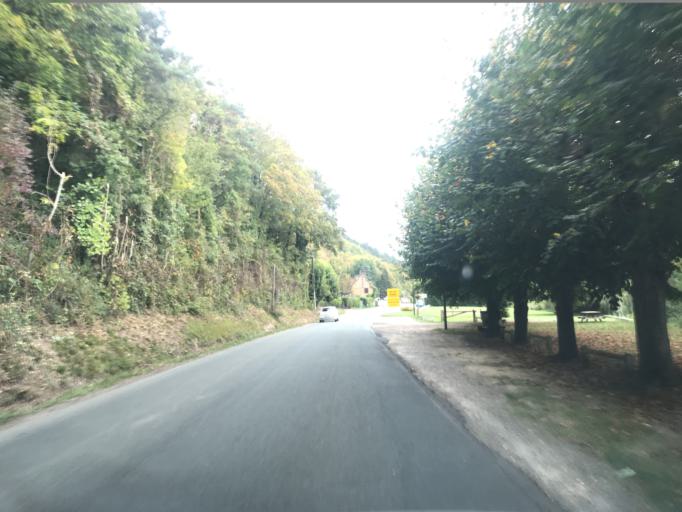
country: FR
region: Haute-Normandie
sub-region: Departement de l'Eure
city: Acquigny
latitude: 49.1759
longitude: 1.1863
